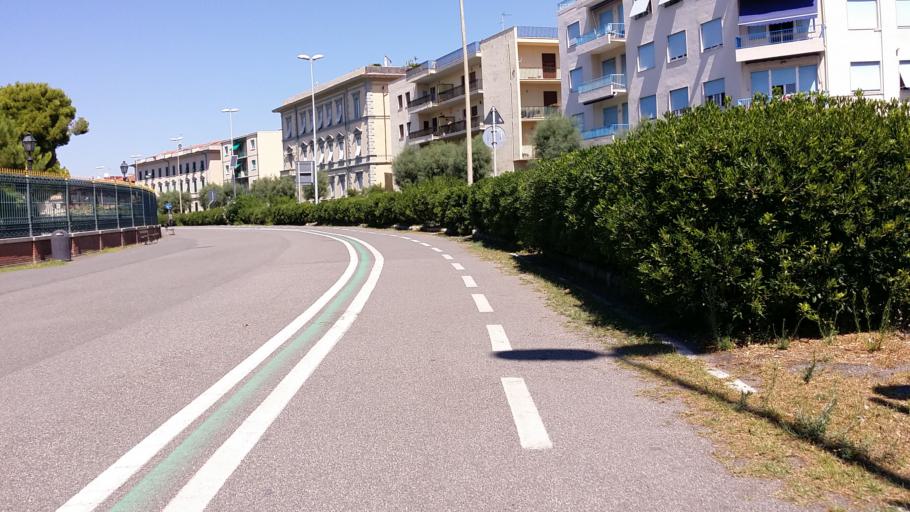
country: IT
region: Tuscany
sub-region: Provincia di Livorno
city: Livorno
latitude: 43.5283
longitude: 10.3098
